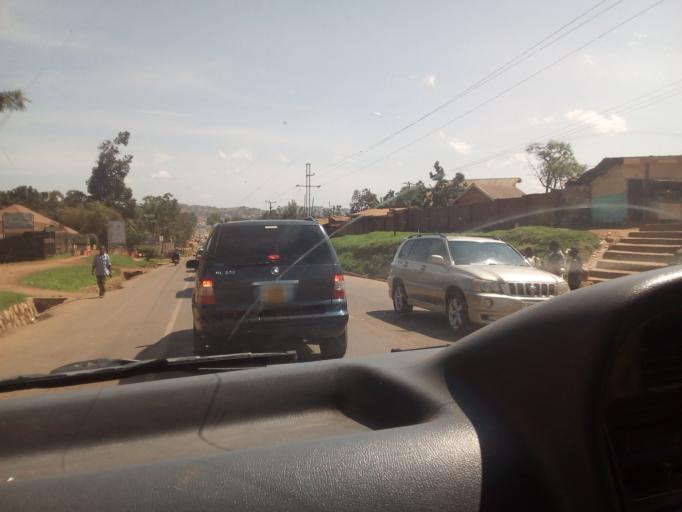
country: UG
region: Central Region
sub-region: Wakiso District
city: Kajansi
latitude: 0.2301
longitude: 32.5509
